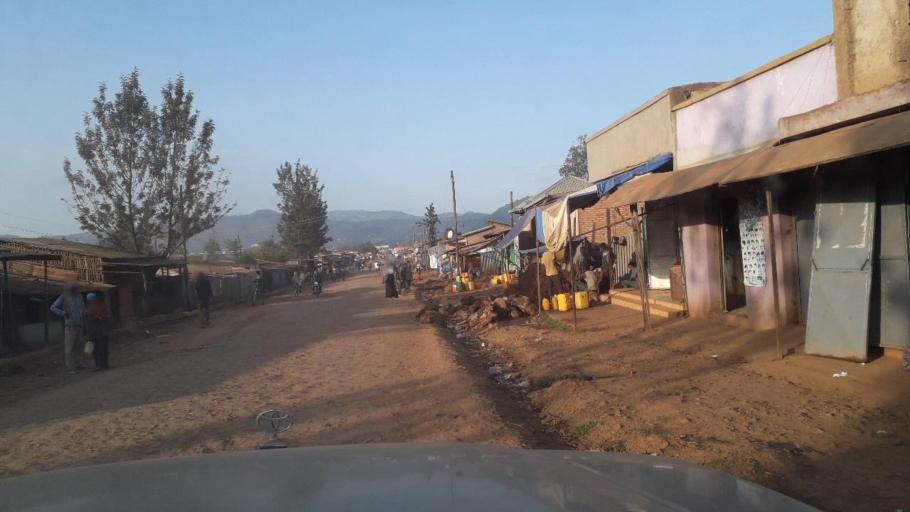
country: ET
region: Oromiya
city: Jima
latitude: 7.6417
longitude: 36.8423
